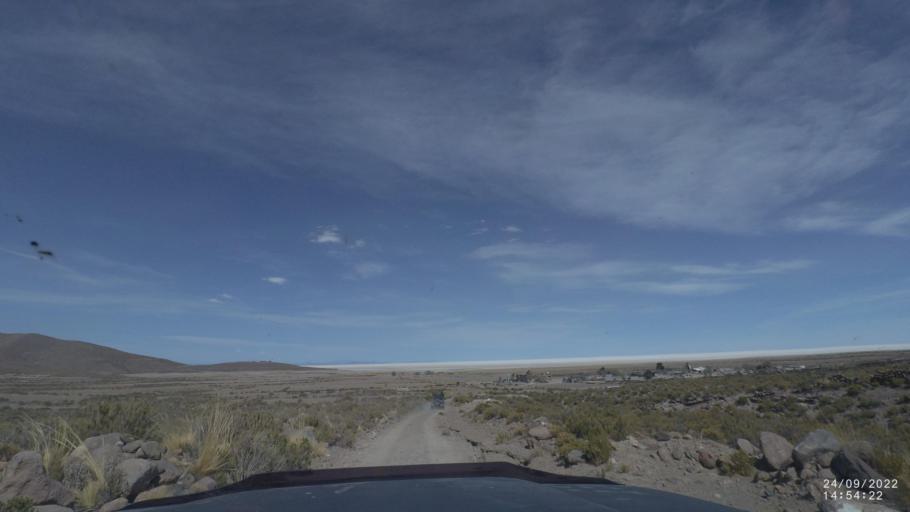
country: BO
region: Potosi
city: Colchani
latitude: -19.8536
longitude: -67.5754
